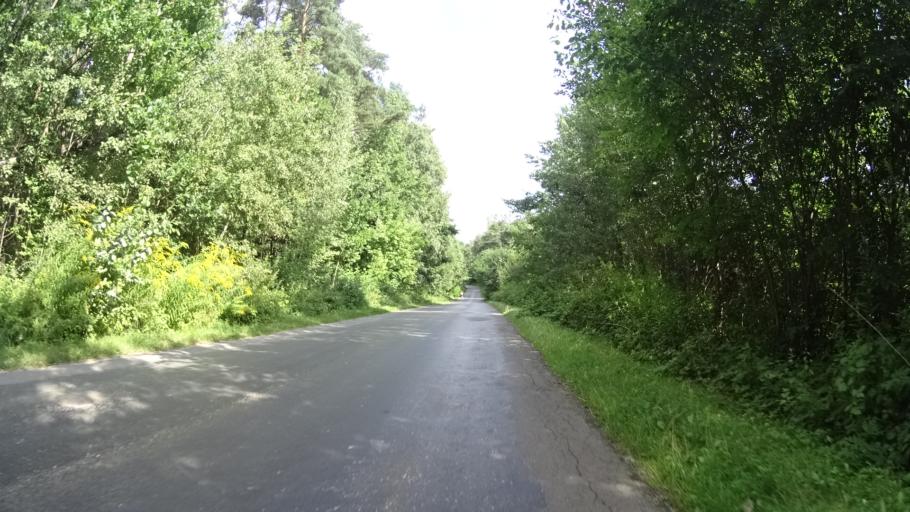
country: PL
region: Masovian Voivodeship
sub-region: Powiat grojecki
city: Mogielnica
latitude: 51.6925
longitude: 20.7368
